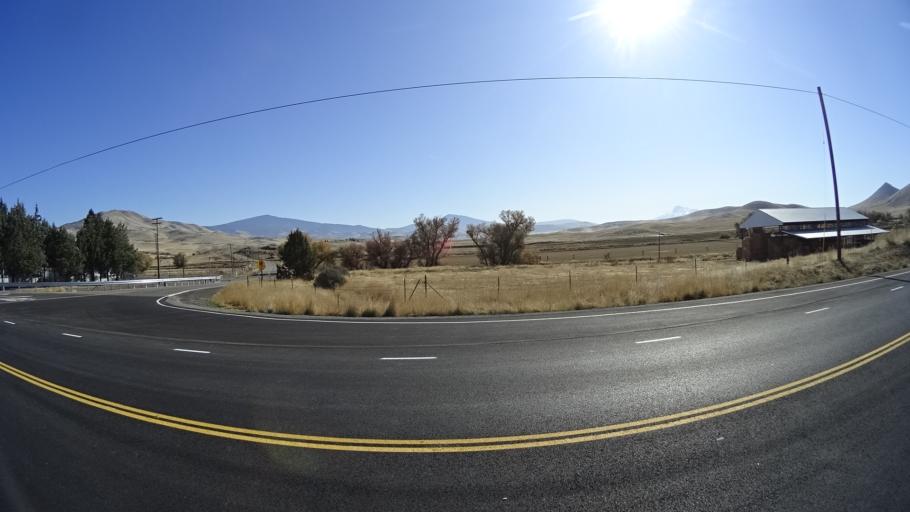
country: US
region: California
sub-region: Siskiyou County
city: Montague
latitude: 41.8485
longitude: -122.4694
